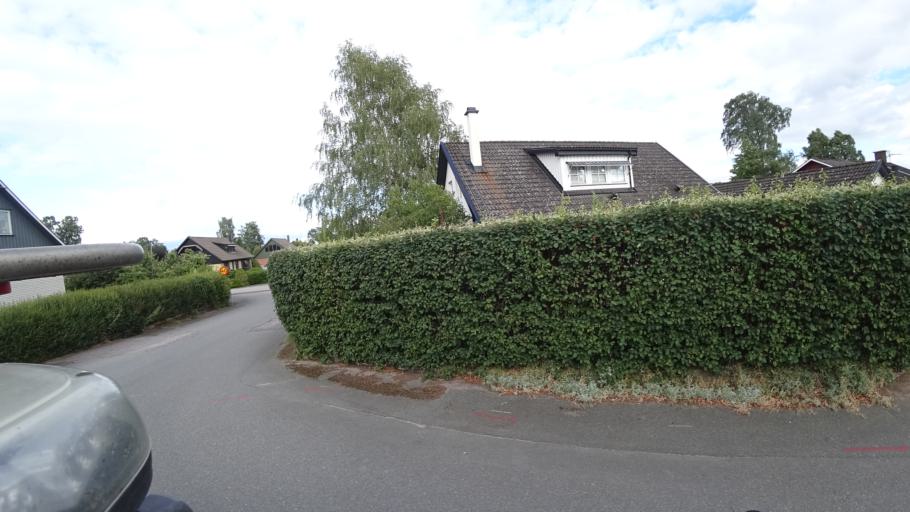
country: SE
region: Skane
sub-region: Ostra Goinge Kommun
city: Knislinge
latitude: 56.1899
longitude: 14.0693
